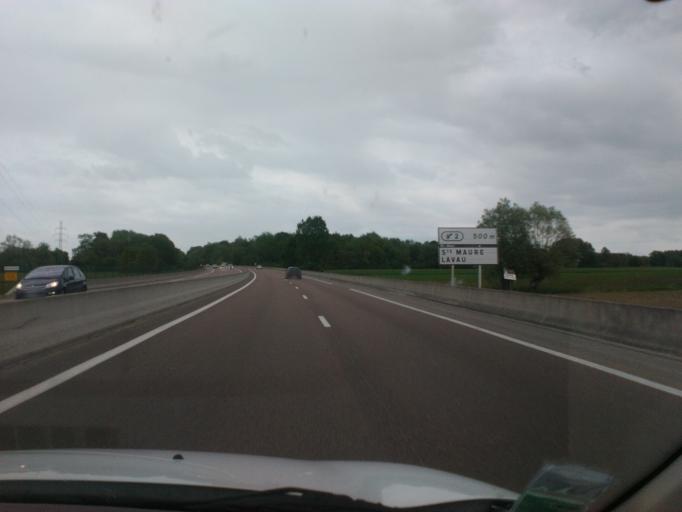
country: FR
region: Champagne-Ardenne
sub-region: Departement de l'Aube
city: Pont-Sainte-Marie
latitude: 48.3276
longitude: 4.0728
